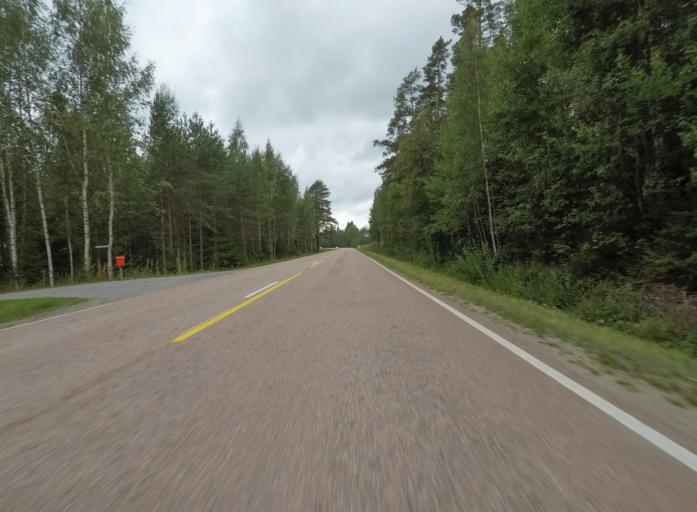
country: FI
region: Central Finland
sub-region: Jyvaeskylae
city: Hankasalmi
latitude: 62.3604
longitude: 26.5476
